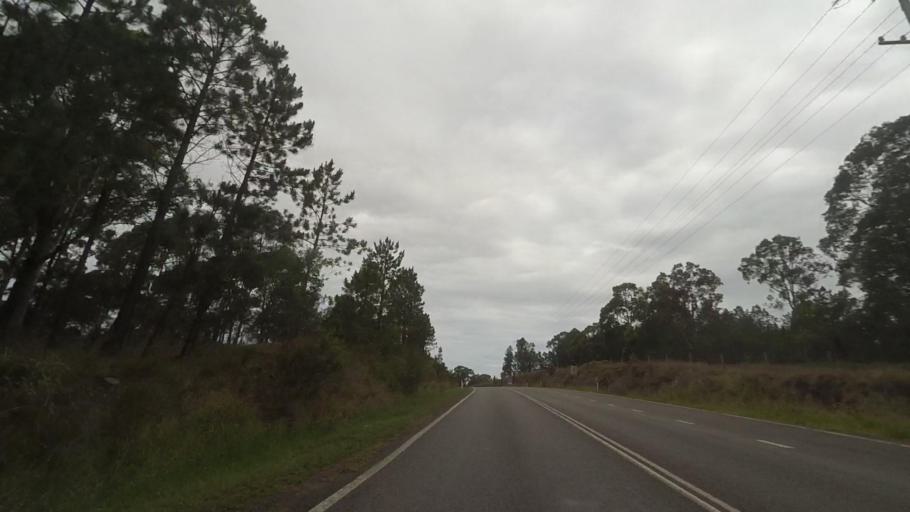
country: AU
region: New South Wales
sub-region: Great Lakes
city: Hawks Nest
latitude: -32.6180
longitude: 152.1119
